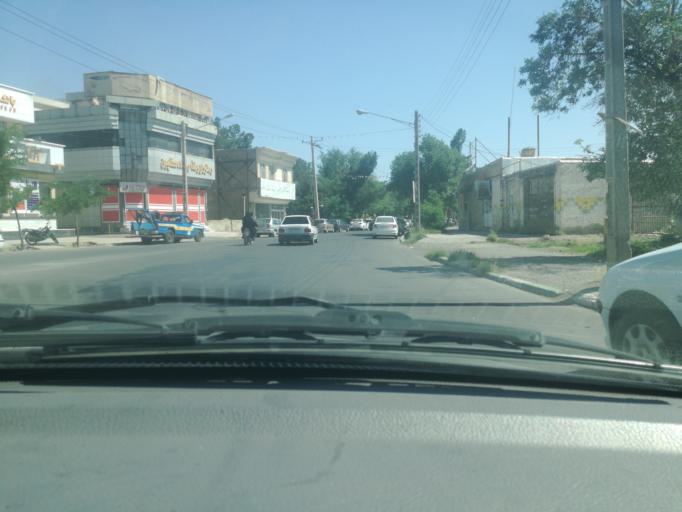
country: IR
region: Razavi Khorasan
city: Sarakhs
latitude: 36.5341
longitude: 61.1619
